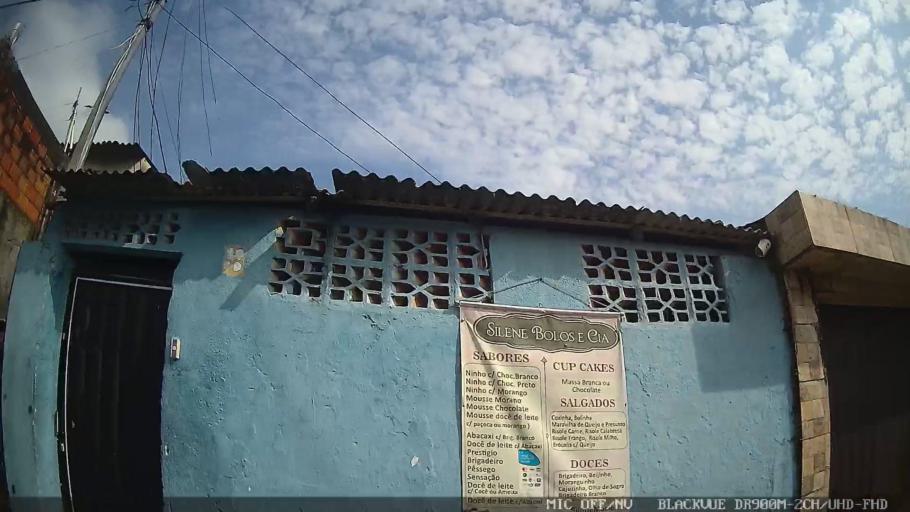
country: BR
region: Sao Paulo
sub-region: Santos
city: Santos
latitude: -23.9506
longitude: -46.2974
